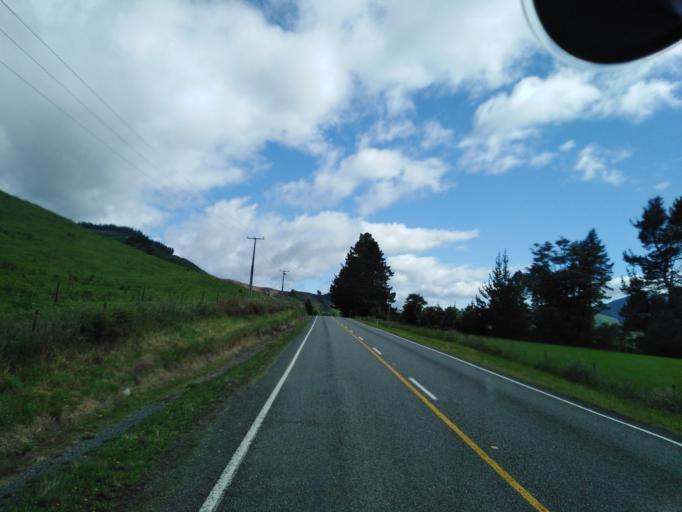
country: NZ
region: Nelson
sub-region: Nelson City
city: Nelson
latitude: -41.2746
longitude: 173.5730
